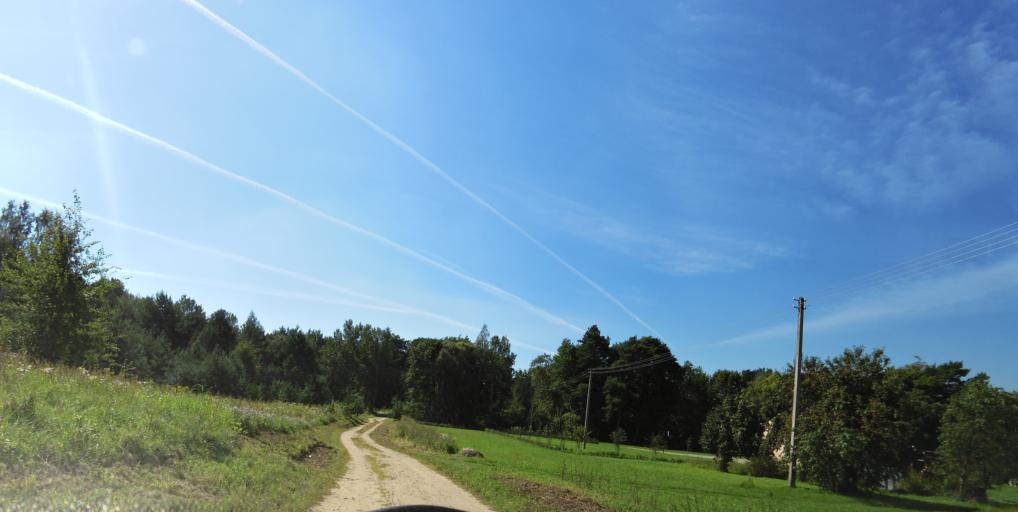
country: LT
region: Vilnius County
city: Rasos
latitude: 54.6831
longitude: 25.3630
